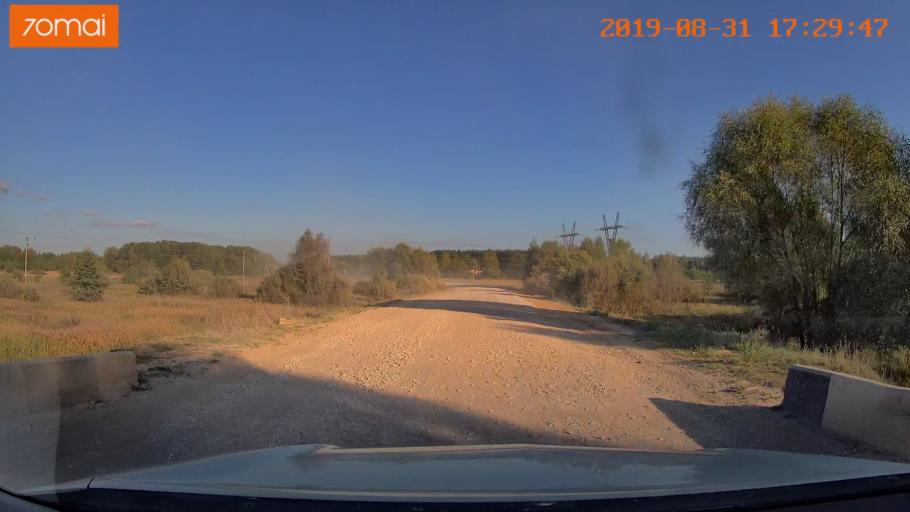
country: RU
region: Kaluga
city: Detchino
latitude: 54.8120
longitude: 36.3282
